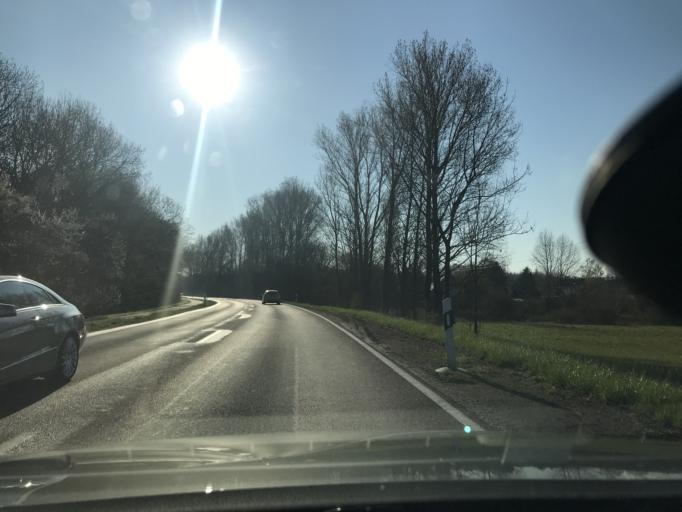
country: DE
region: Saxony-Anhalt
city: Holleben
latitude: 51.4283
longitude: 11.9109
